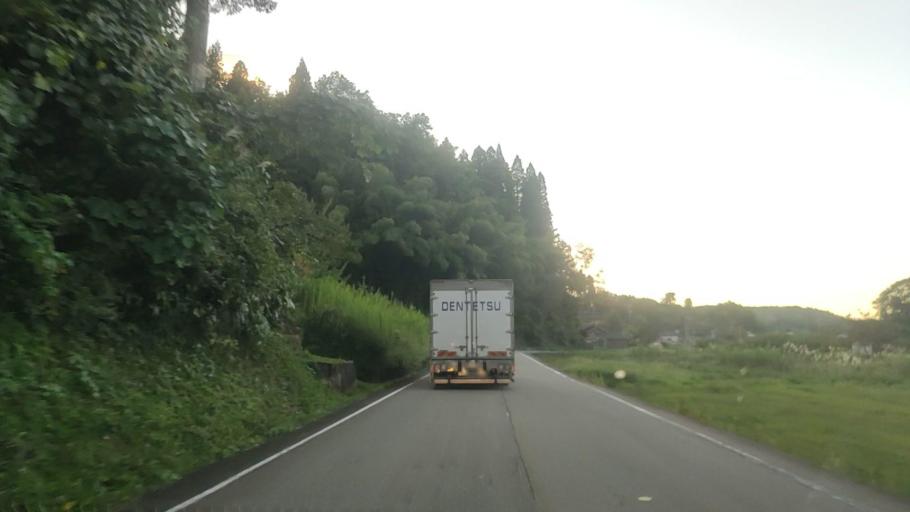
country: JP
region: Ishikawa
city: Tsubata
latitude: 36.6437
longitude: 136.7666
